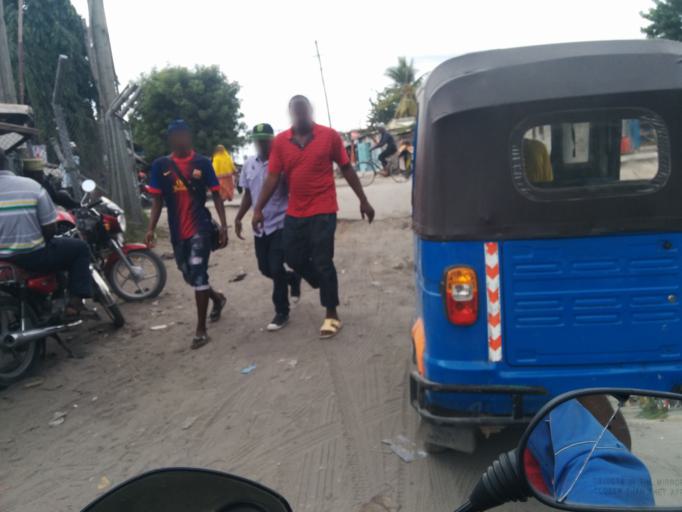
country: TZ
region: Dar es Salaam
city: Dar es Salaam
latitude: -6.8654
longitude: 39.2560
